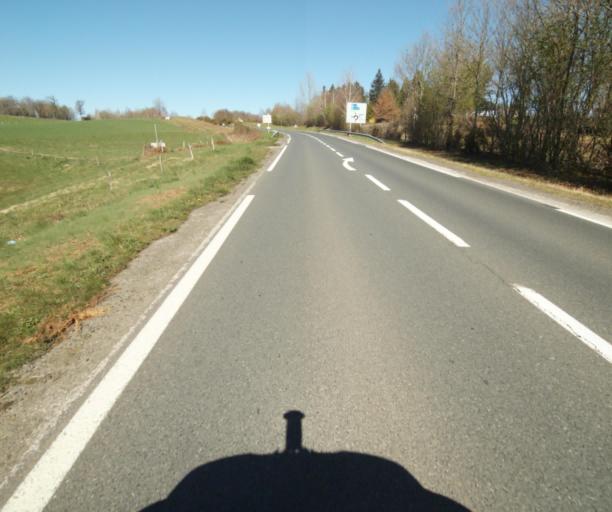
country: FR
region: Limousin
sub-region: Departement de la Correze
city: Seilhac
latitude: 45.3537
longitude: 1.7342
